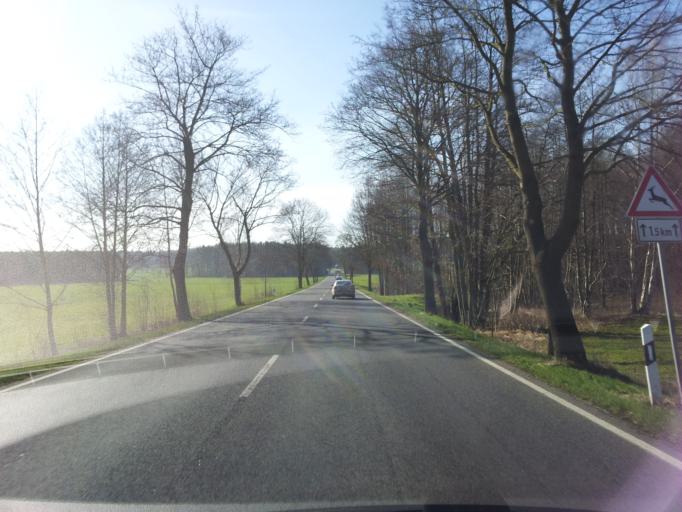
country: DE
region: Saxony
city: Konigsbruck
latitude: 51.2864
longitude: 13.9050
